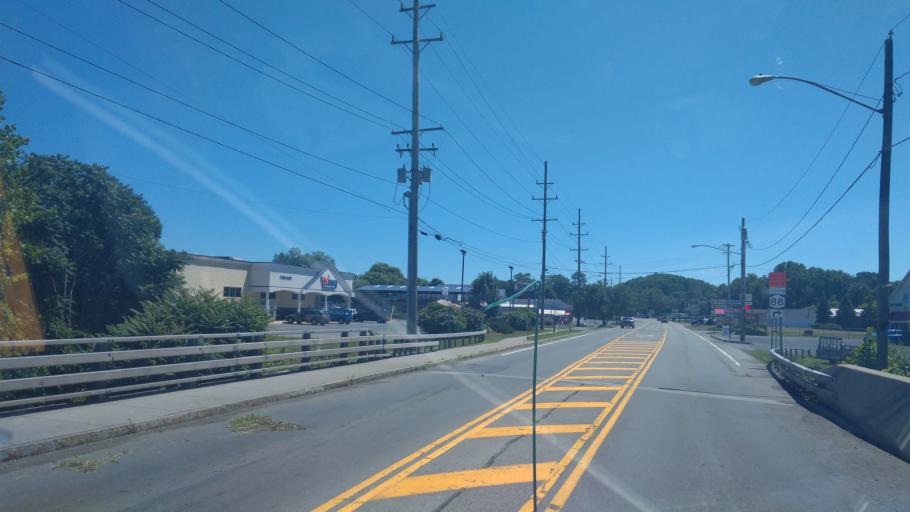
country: US
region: New York
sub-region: Wayne County
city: Lyons
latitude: 43.0606
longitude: -76.9973
